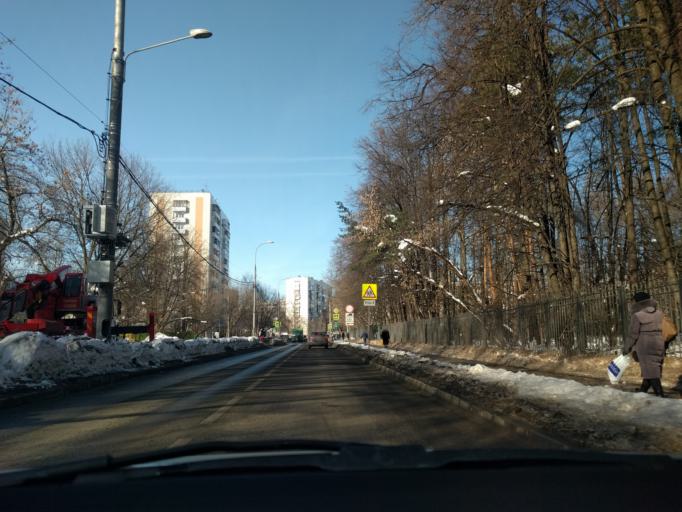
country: RU
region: Moskovskaya
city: Izmaylovo
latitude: 55.7959
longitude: 37.8235
